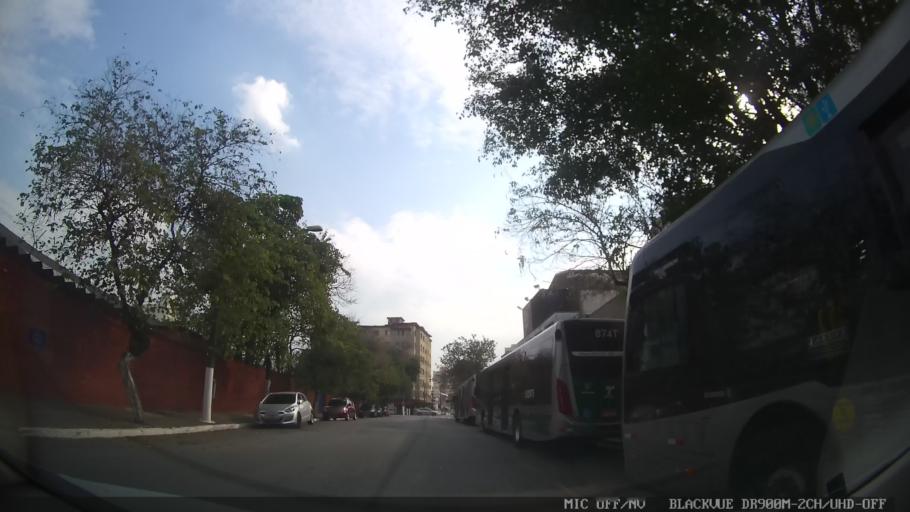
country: BR
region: Sao Paulo
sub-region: Sao Paulo
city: Sao Paulo
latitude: -23.5779
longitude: -46.6015
